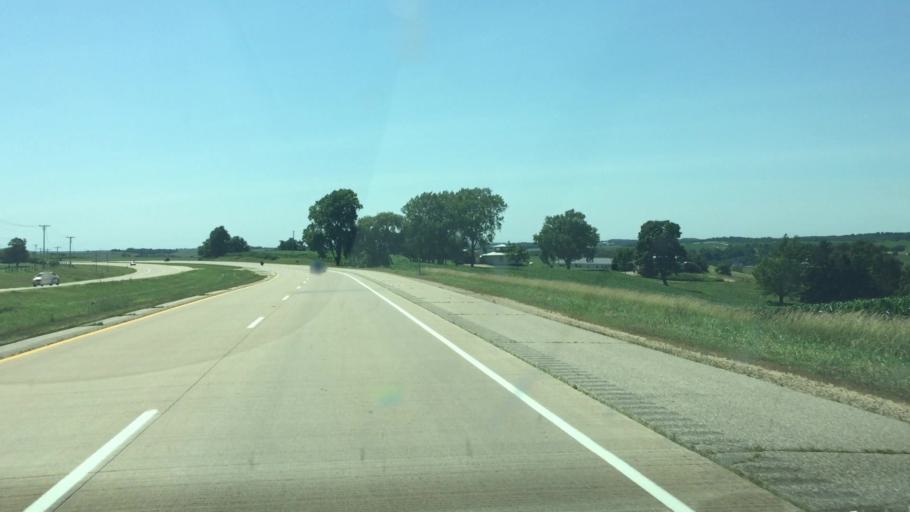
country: US
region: Wisconsin
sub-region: Iowa County
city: Mineral Point
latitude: 42.8403
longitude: -90.2139
